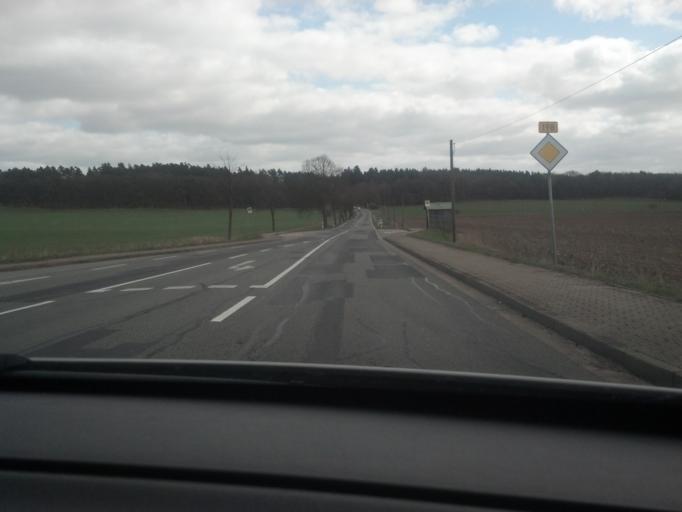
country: DE
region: Mecklenburg-Vorpommern
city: Malchow
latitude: 53.3658
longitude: 12.3827
